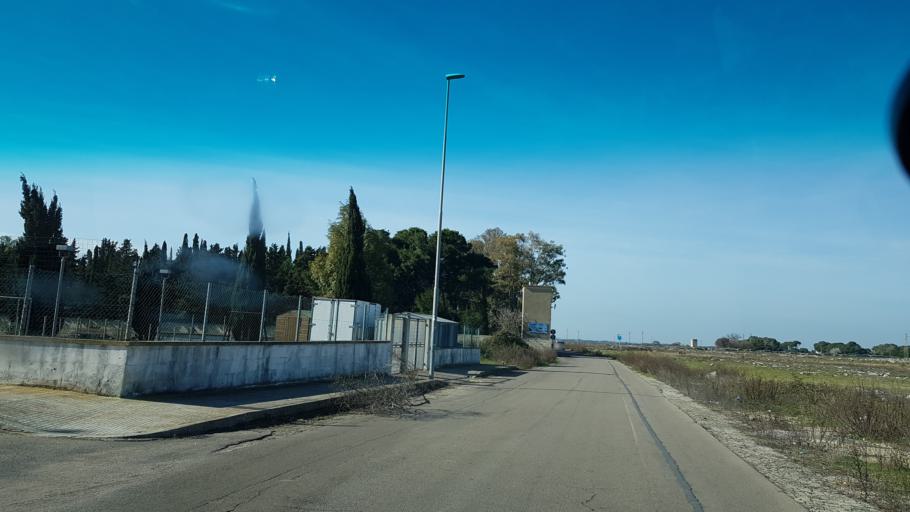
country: IT
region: Apulia
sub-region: Provincia di Lecce
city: Lecce
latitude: 40.3494
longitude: 18.1438
